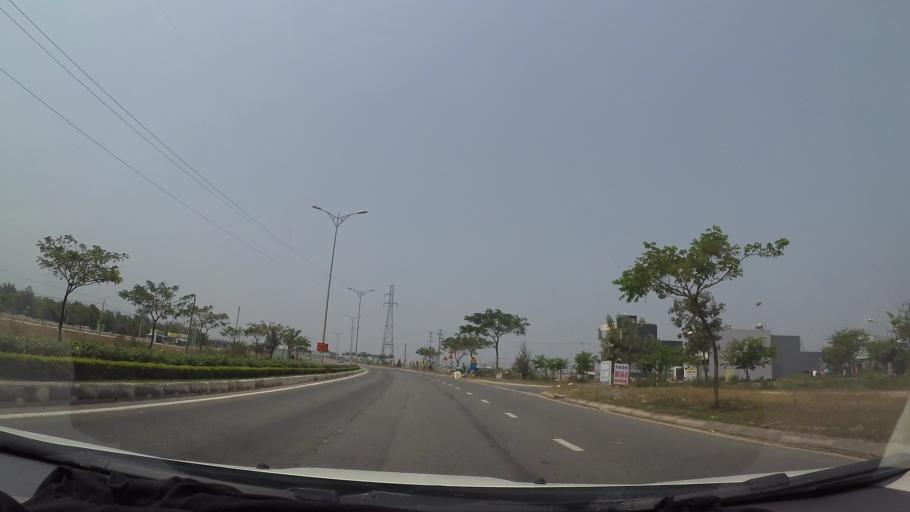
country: VN
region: Da Nang
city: Ngu Hanh Son
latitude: 15.9983
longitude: 108.2337
